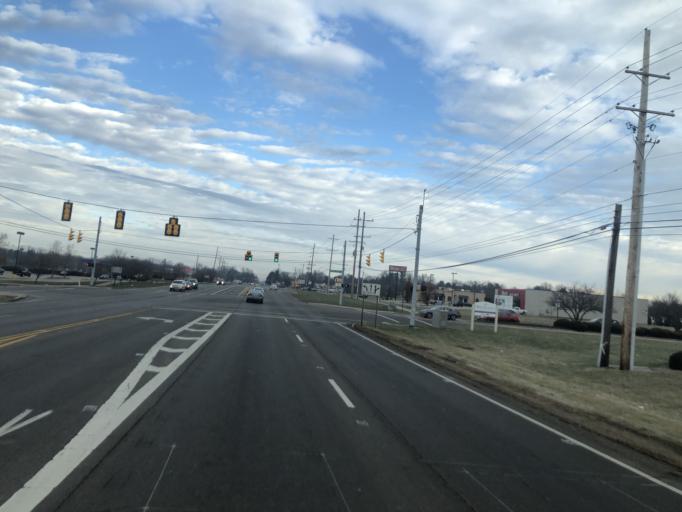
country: US
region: Ohio
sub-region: Franklin County
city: Groveport
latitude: 39.8947
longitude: -82.8825
